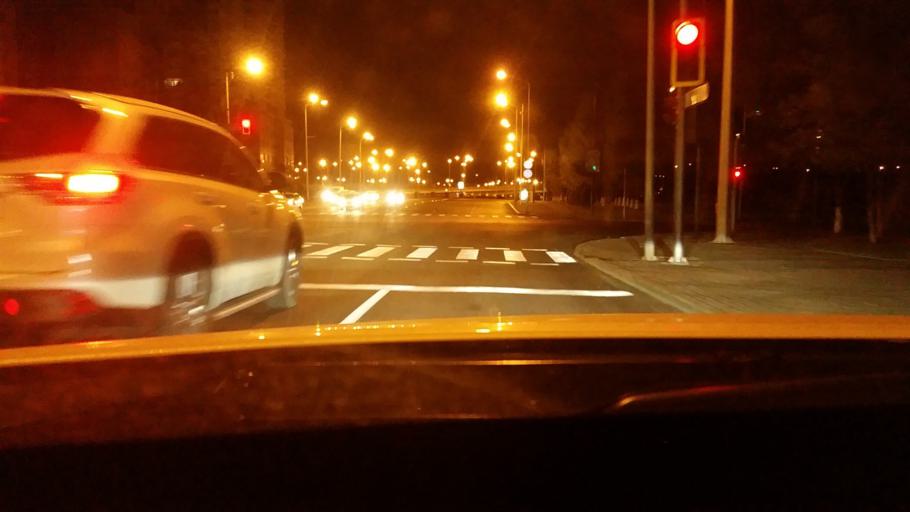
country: KZ
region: Astana Qalasy
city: Astana
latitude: 51.1291
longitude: 71.4394
